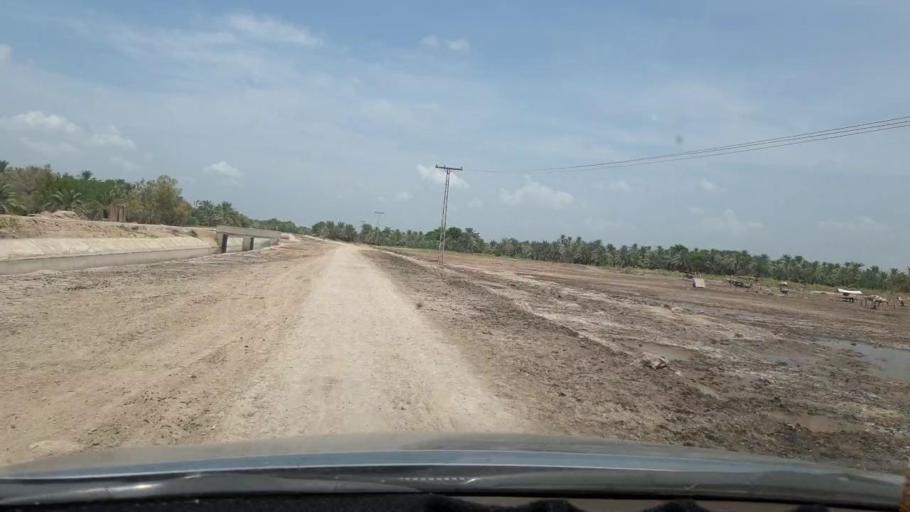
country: PK
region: Sindh
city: Khairpur
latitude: 27.4353
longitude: 68.7818
